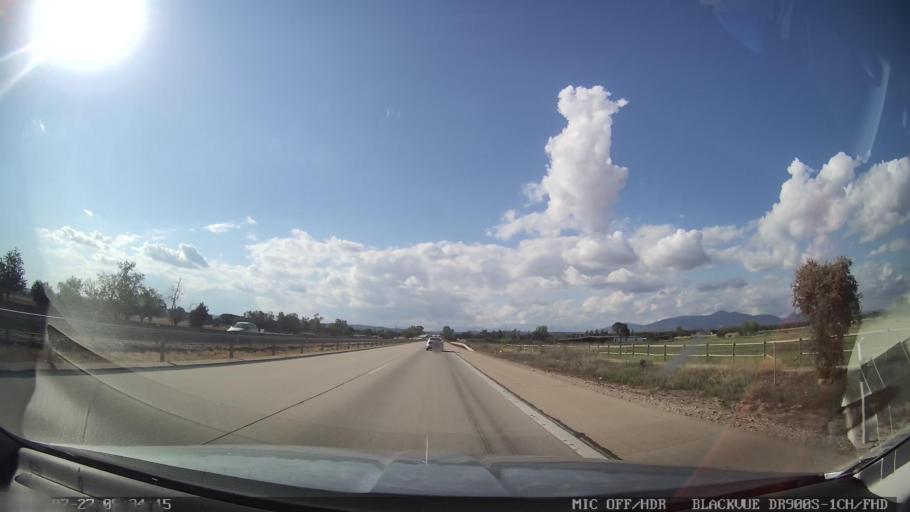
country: ES
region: Castille-La Mancha
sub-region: Province of Toledo
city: Talavera de la Reina
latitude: 39.9916
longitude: -4.7584
